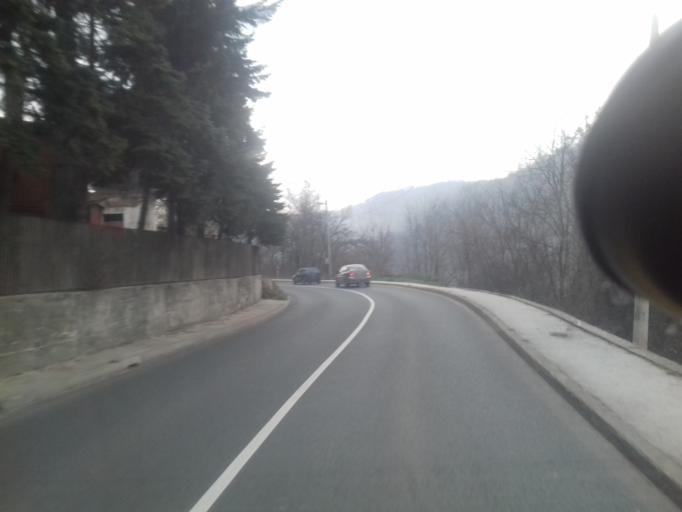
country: BA
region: Federation of Bosnia and Herzegovina
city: Ilijas
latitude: 43.9287
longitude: 18.3040
